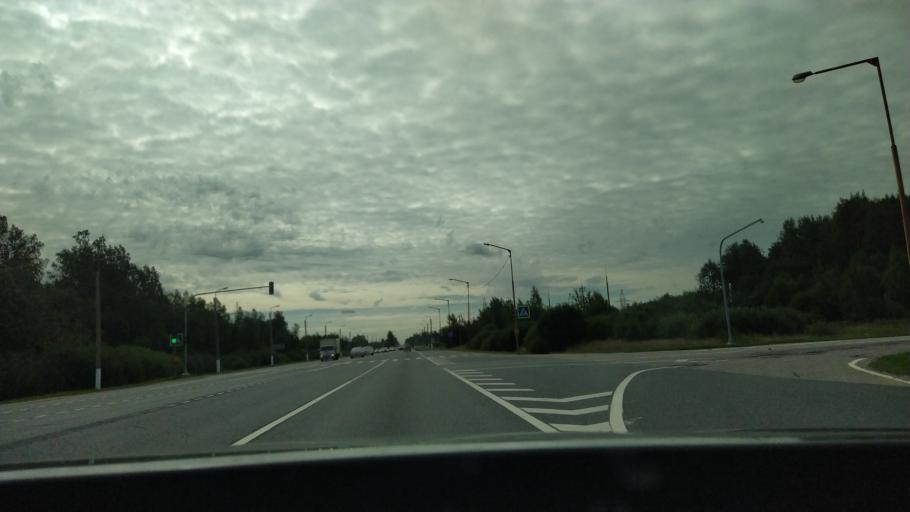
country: RU
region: Leningrad
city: Tosno
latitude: 59.5686
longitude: 30.8266
